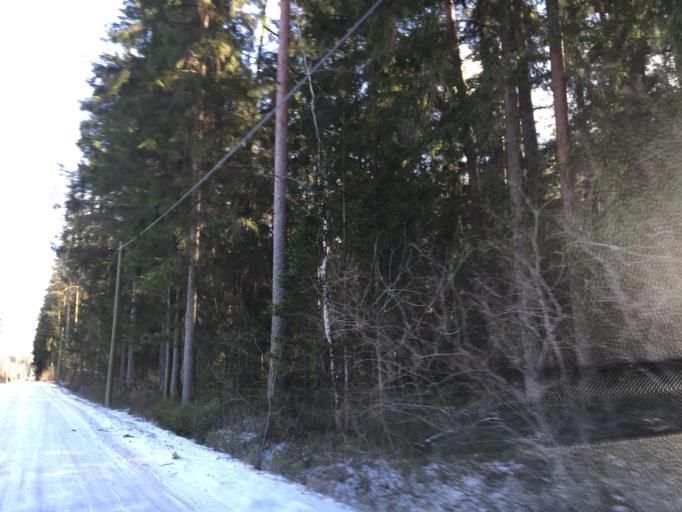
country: LV
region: Garkalne
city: Garkalne
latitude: 56.9517
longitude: 24.4449
